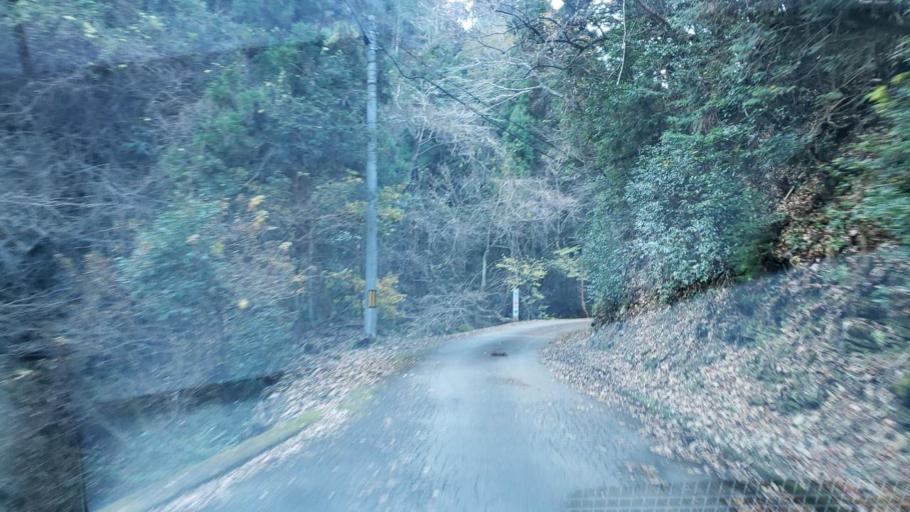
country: JP
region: Tokushima
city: Wakimachi
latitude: 33.9875
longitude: 133.9856
